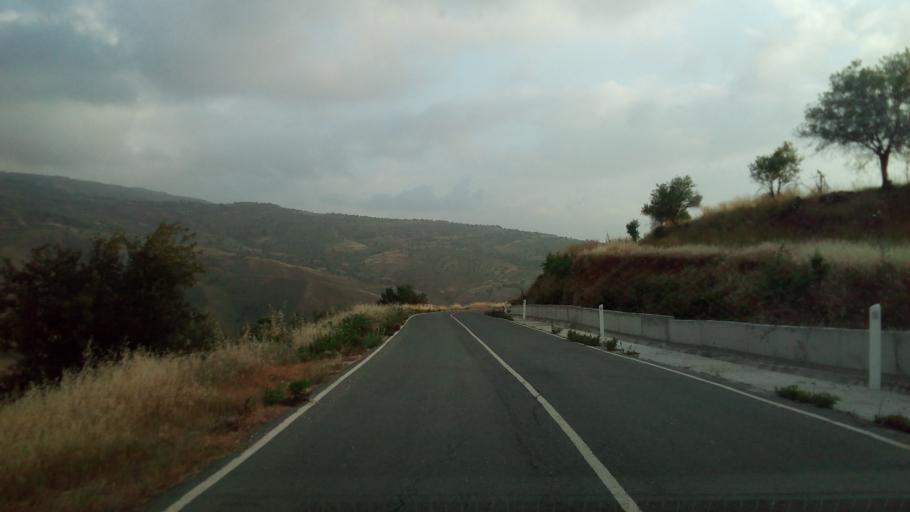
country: CY
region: Limassol
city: Pachna
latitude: 34.8362
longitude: 32.6625
